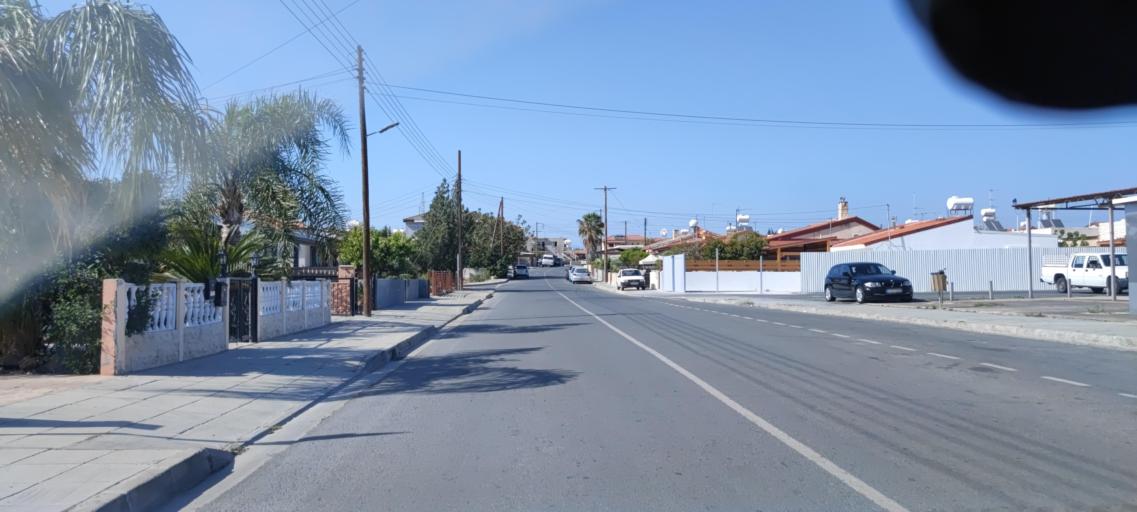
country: CY
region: Larnaka
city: Kolossi
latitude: 34.6588
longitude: 32.9563
